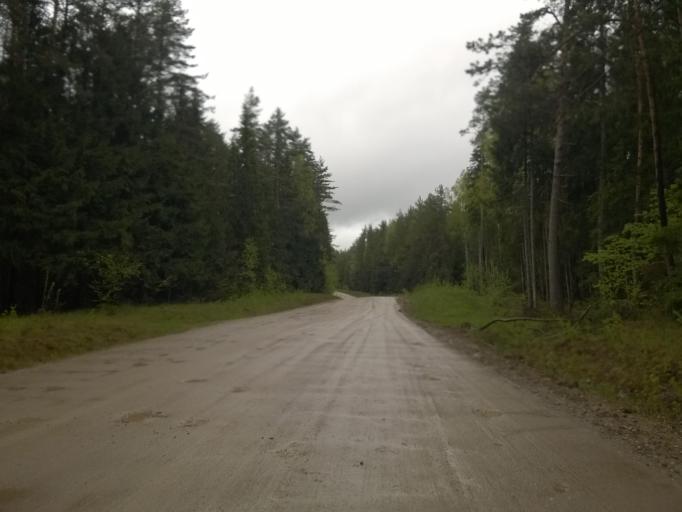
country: LV
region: Amatas Novads
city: Drabesi
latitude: 57.2105
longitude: 25.2352
